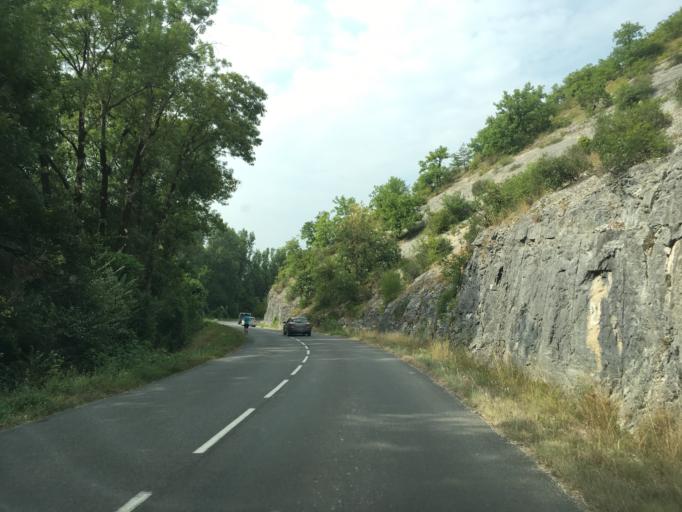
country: FR
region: Midi-Pyrenees
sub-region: Departement du Lot
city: Souillac
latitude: 44.8693
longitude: 1.4986
